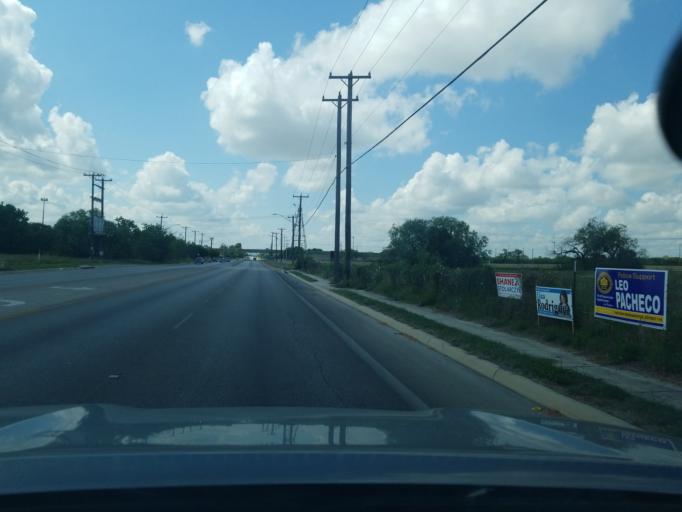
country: US
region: Texas
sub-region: Bexar County
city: Lackland Air Force Base
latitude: 29.3237
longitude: -98.5327
